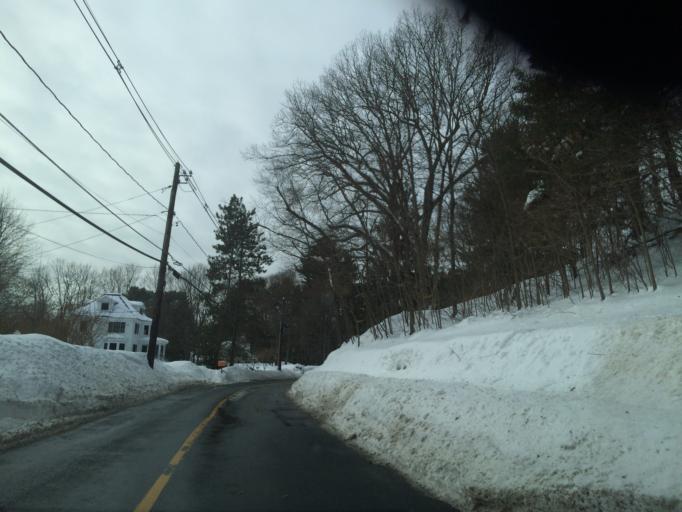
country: US
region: Massachusetts
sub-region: Middlesex County
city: Weston
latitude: 42.3942
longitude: -71.3025
